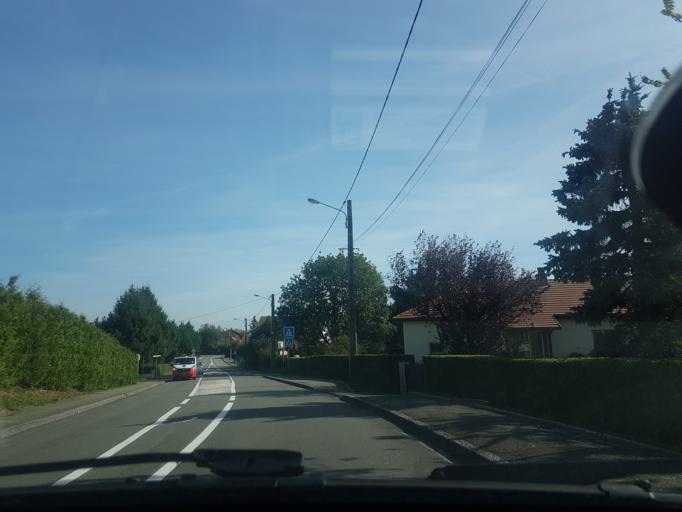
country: FR
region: Franche-Comte
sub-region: Territoire de Belfort
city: Offemont
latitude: 47.6679
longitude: 6.9118
